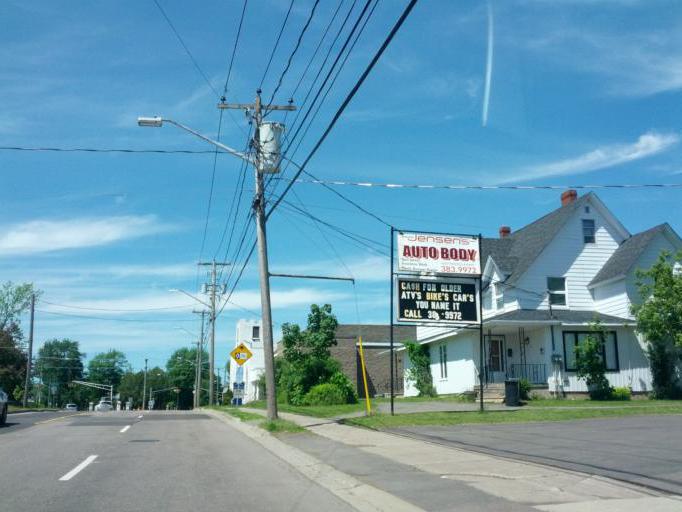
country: CA
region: New Brunswick
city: Moncton
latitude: 46.1043
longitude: -64.7740
